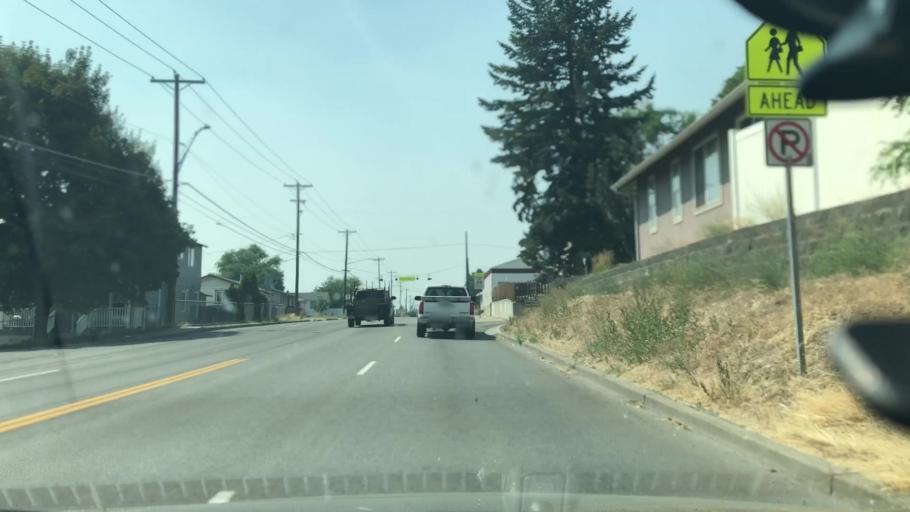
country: US
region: Washington
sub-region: Spokane County
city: Spokane
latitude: 47.6862
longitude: -117.3717
